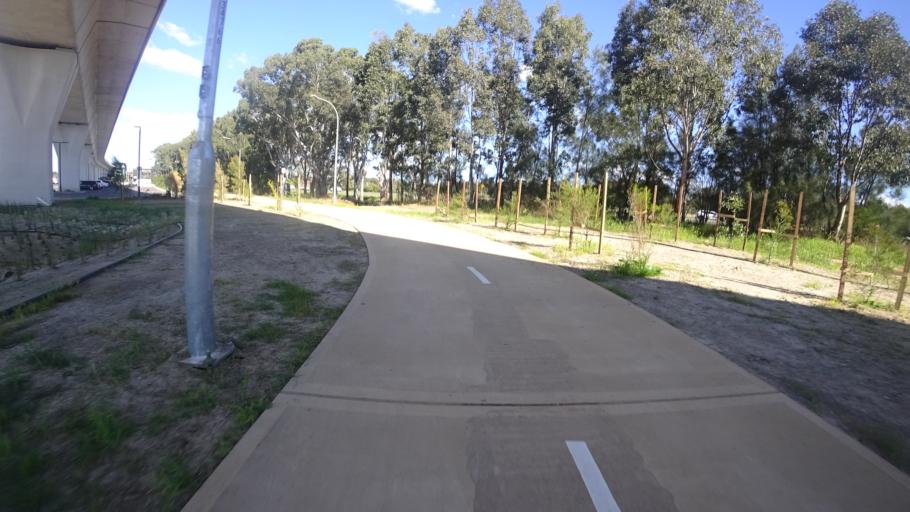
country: AU
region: New South Wales
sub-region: Blacktown
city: Stanhope Gardens
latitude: -33.7095
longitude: 150.9331
